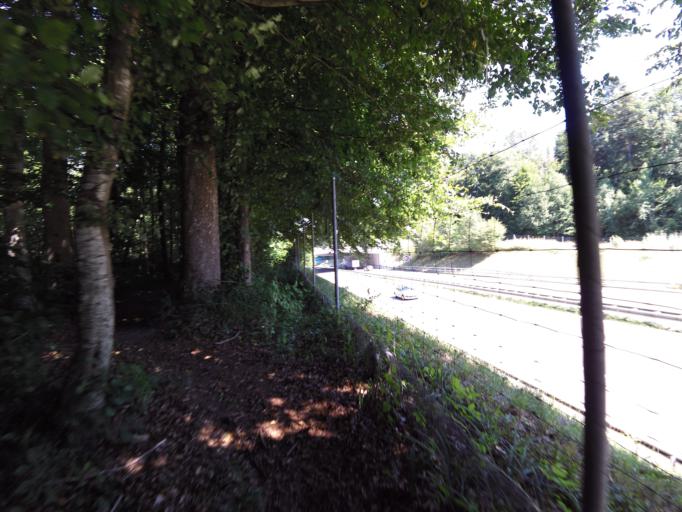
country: CH
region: Thurgau
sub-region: Kreuzlingen District
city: Tagerwilen
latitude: 47.6301
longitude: 9.1430
